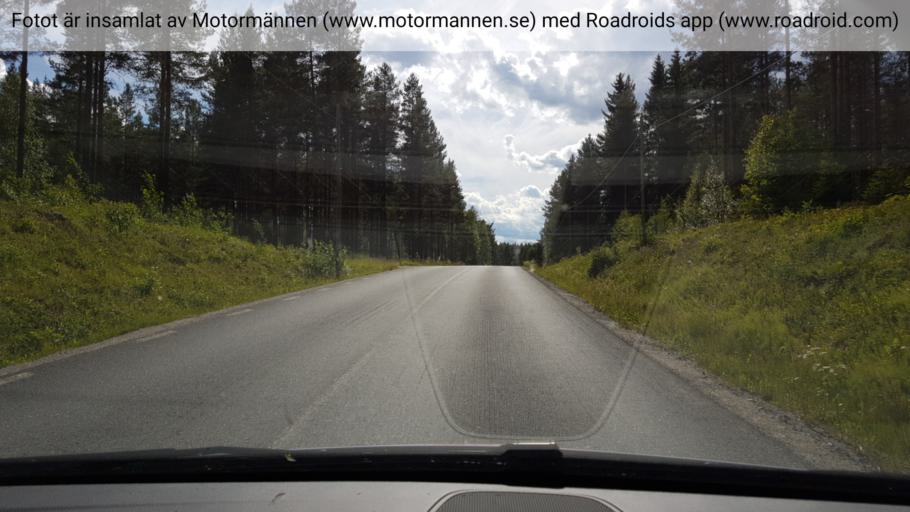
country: SE
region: Jaemtland
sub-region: Braecke Kommun
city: Braecke
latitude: 62.3950
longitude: 15.1445
